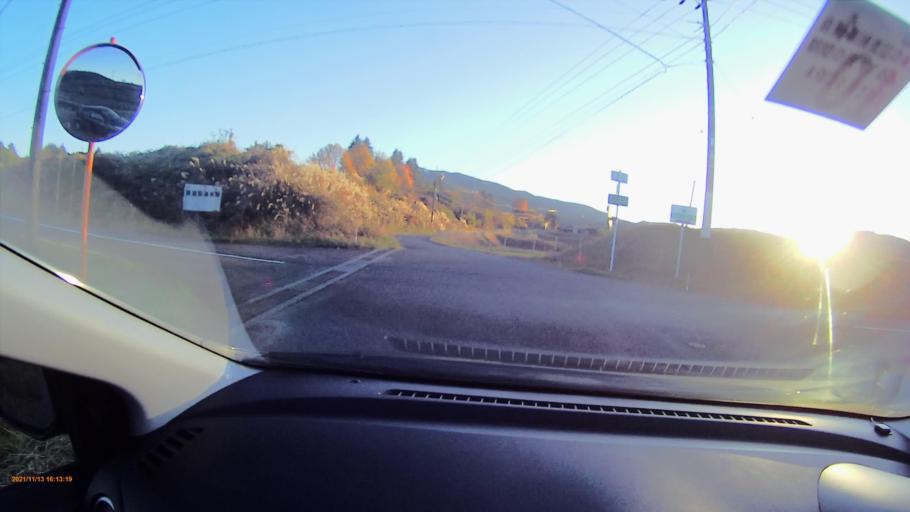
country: JP
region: Gifu
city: Nakatsugawa
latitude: 35.5792
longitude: 137.5108
